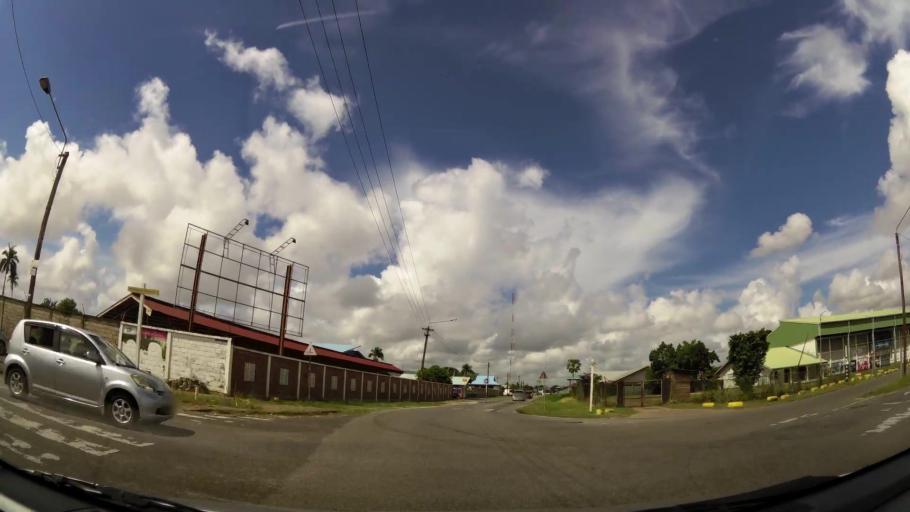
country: SR
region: Paramaribo
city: Paramaribo
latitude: 5.8273
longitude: -55.1759
